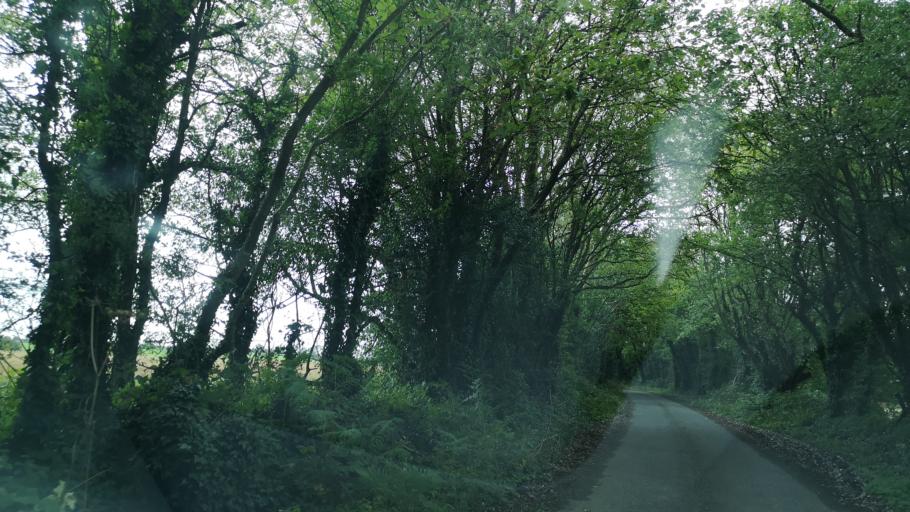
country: IE
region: Connaught
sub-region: County Galway
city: Athenry
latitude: 53.3118
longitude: -8.7941
